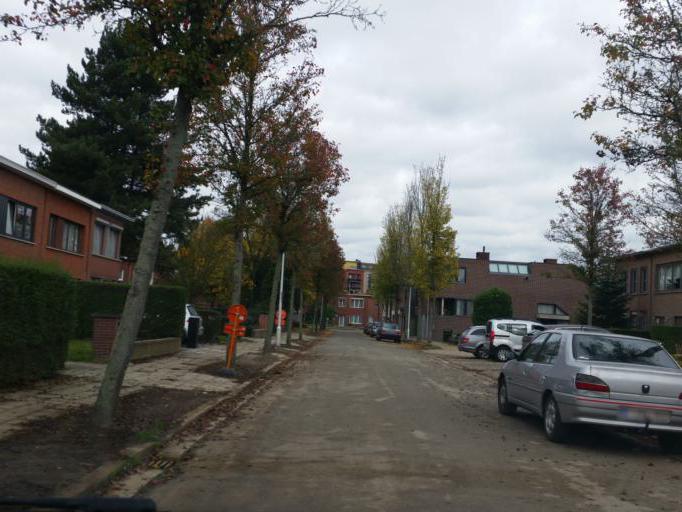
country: BE
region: Flanders
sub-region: Provincie Antwerpen
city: Mortsel
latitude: 51.1664
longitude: 4.4418
